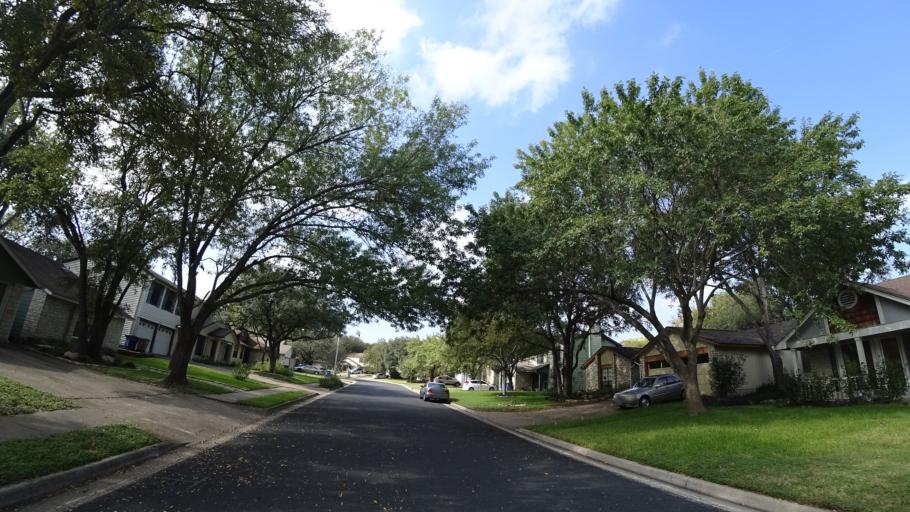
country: US
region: Texas
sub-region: Travis County
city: Shady Hollow
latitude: 30.2012
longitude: -97.8236
